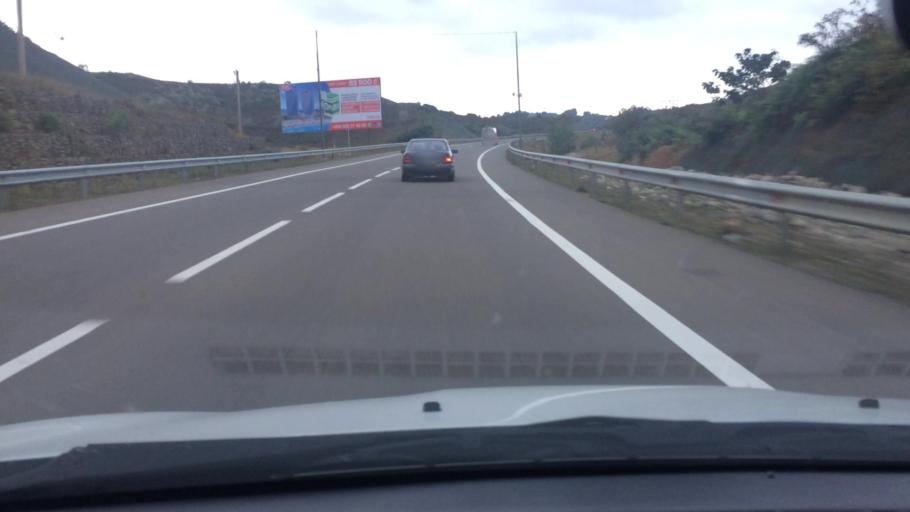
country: GE
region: Ajaria
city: Makhinjauri
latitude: 41.7244
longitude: 41.7494
